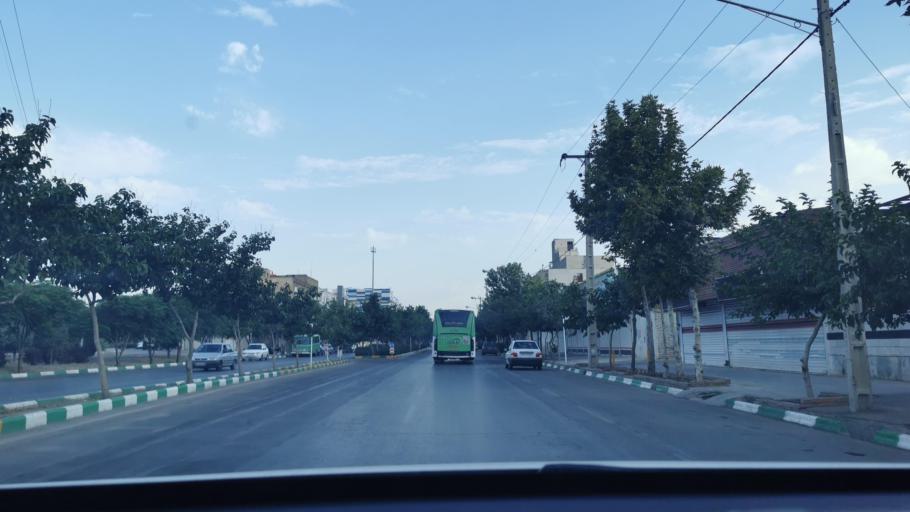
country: IR
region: Razavi Khorasan
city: Mashhad
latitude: 36.3550
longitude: 59.5272
